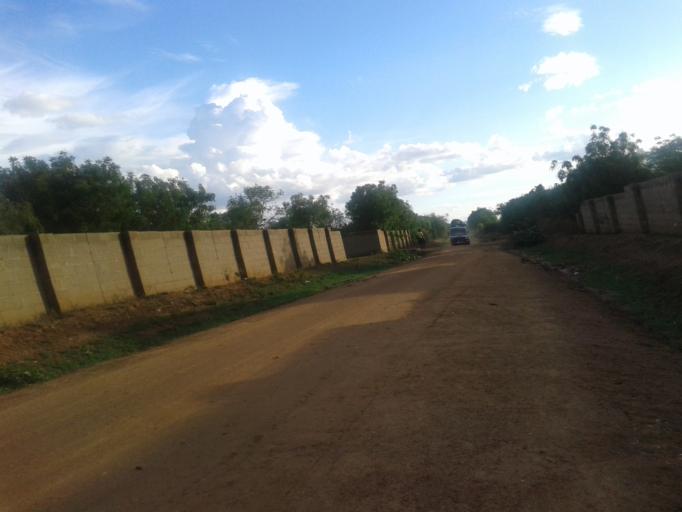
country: UG
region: Northern Region
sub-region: Kotido District
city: Kotido
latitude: 3.0006
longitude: 34.1069
